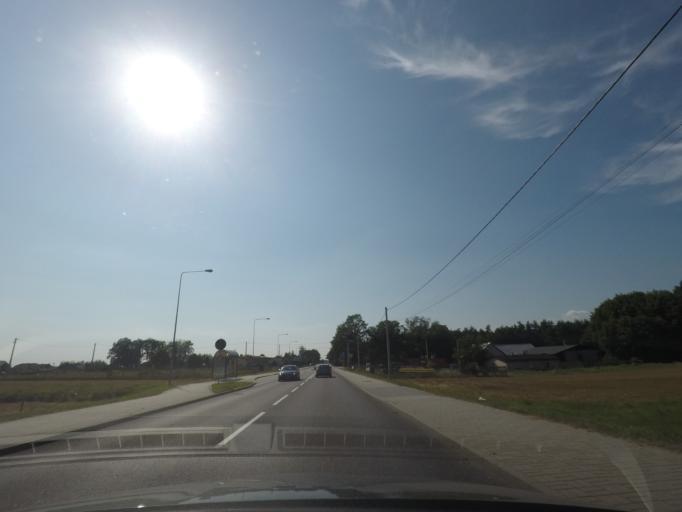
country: PL
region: Silesian Voivodeship
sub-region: Powiat pszczynski
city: Rudziczka
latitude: 50.0384
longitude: 18.7436
